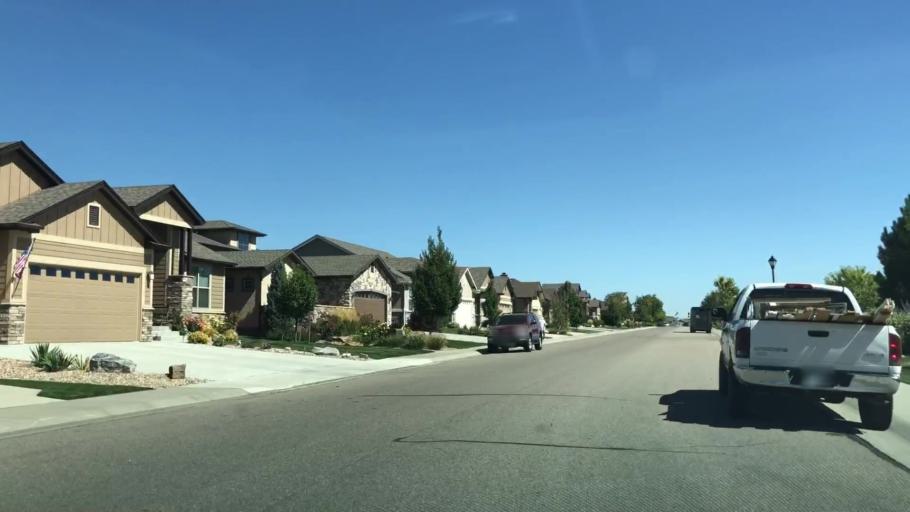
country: US
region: Colorado
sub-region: Weld County
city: Johnstown
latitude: 40.3993
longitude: -104.9805
